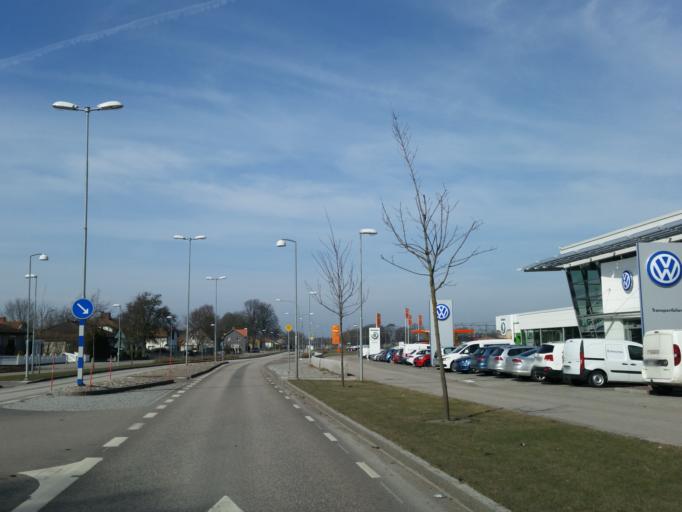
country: SE
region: Kalmar
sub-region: Kalmar Kommun
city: Kalmar
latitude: 56.6658
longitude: 16.3294
